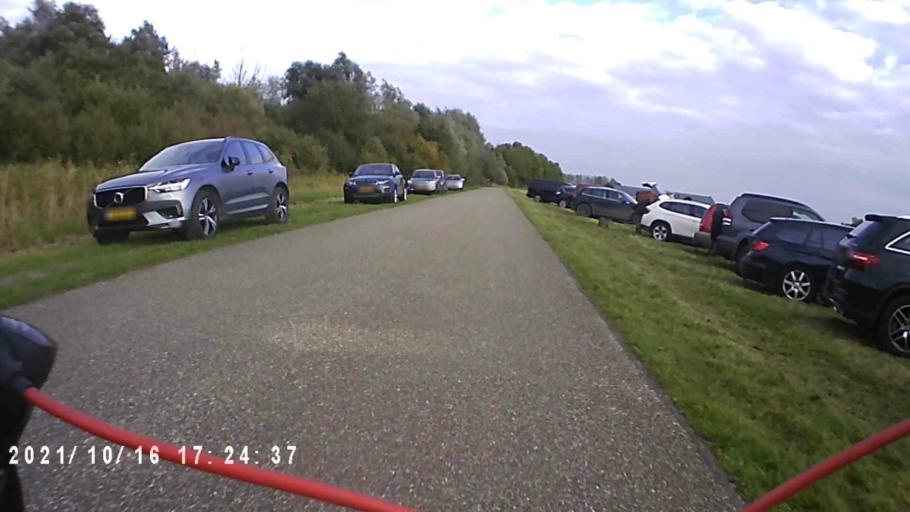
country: NL
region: Friesland
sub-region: Gemeente Kollumerland en Nieuwkruisland
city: Kollum
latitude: 53.3213
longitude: 6.1845
